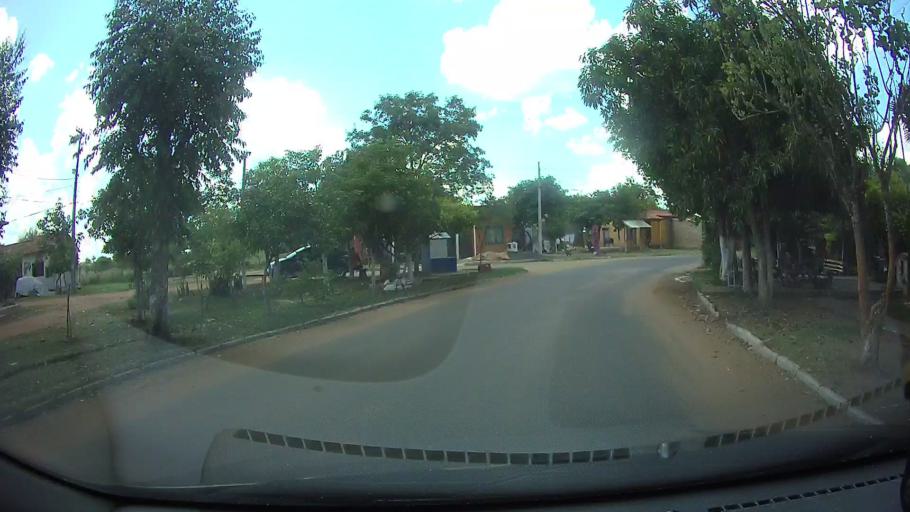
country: PY
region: Central
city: Limpio
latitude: -25.1655
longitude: -57.4315
